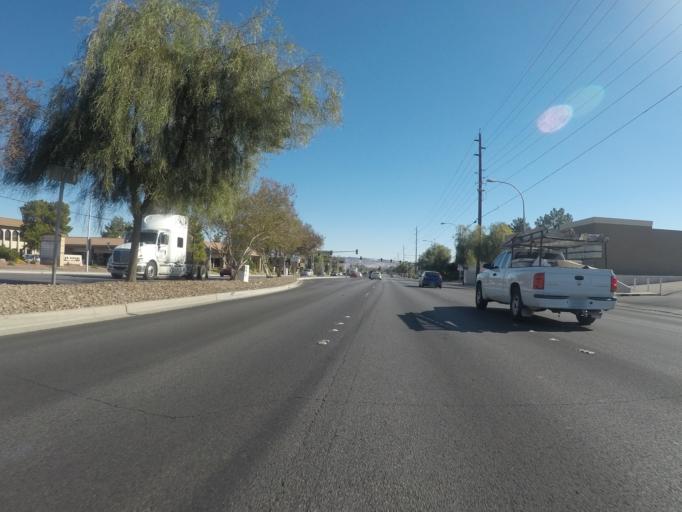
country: US
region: Nevada
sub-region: Clark County
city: Winchester
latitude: 36.1443
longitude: -115.1248
